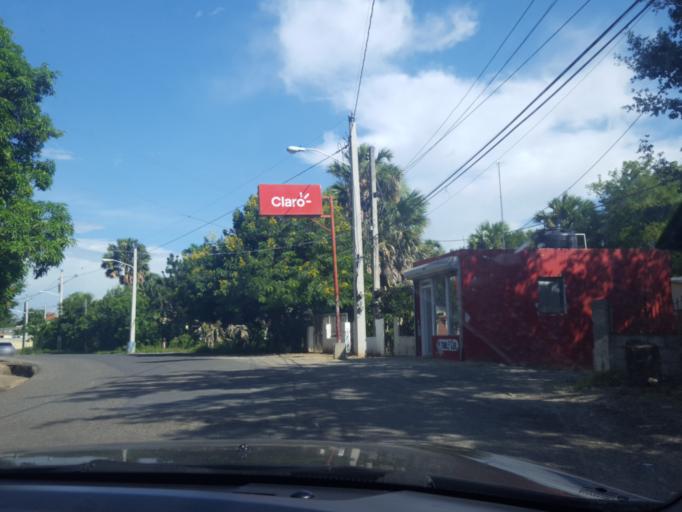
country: DO
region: Santiago
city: Licey al Medio
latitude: 19.3681
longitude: -70.6066
